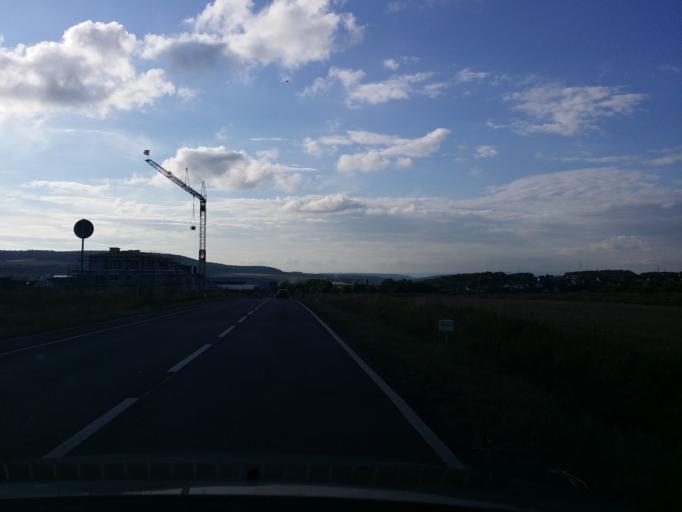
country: DE
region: Hesse
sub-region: Regierungsbezirk Darmstadt
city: Idstein
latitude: 50.2103
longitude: 8.2785
